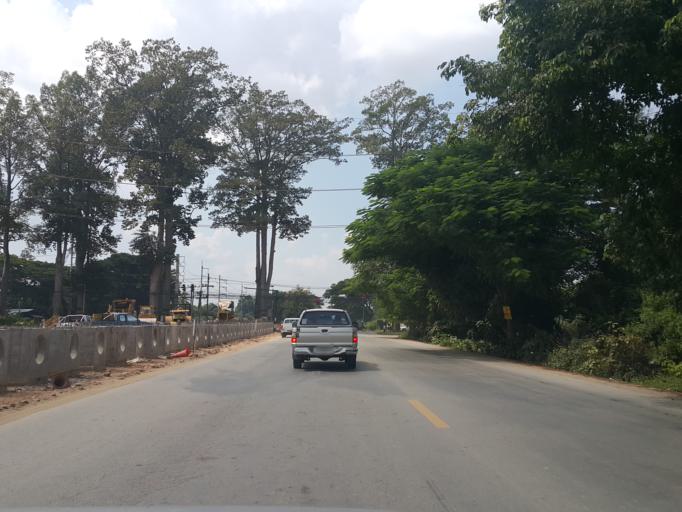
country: TH
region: Chiang Mai
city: Saraphi
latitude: 18.7297
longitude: 99.0244
